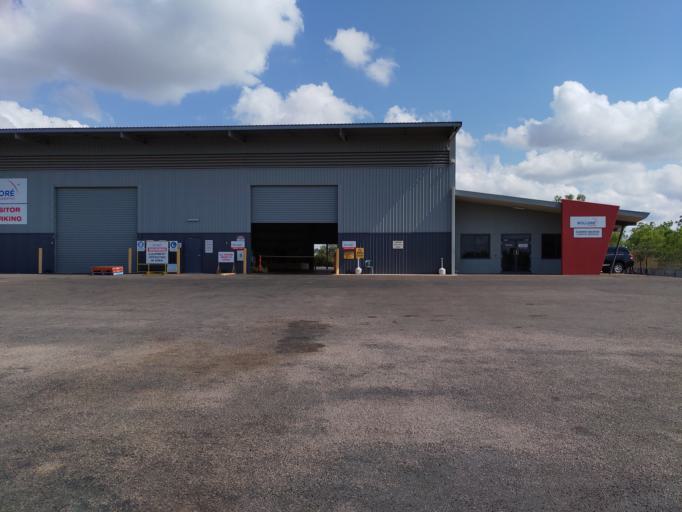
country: AU
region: Northern Territory
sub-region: Palmerston
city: Palmerston
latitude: -12.4784
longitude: 130.9223
